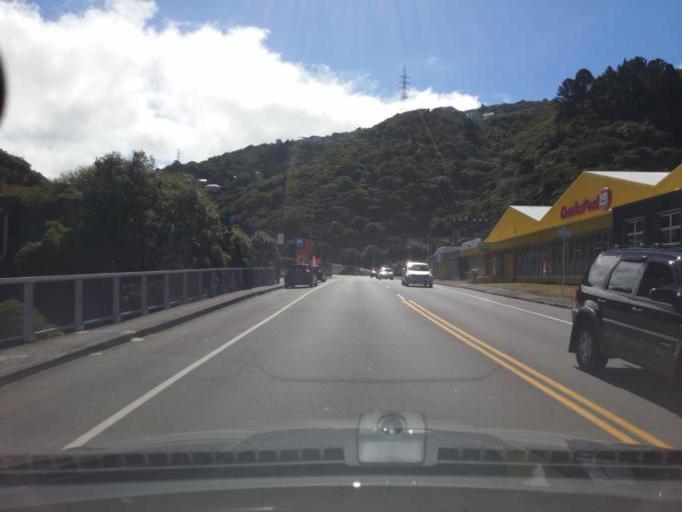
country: NZ
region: Wellington
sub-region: Wellington City
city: Wellington
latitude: -41.2589
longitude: 174.7880
